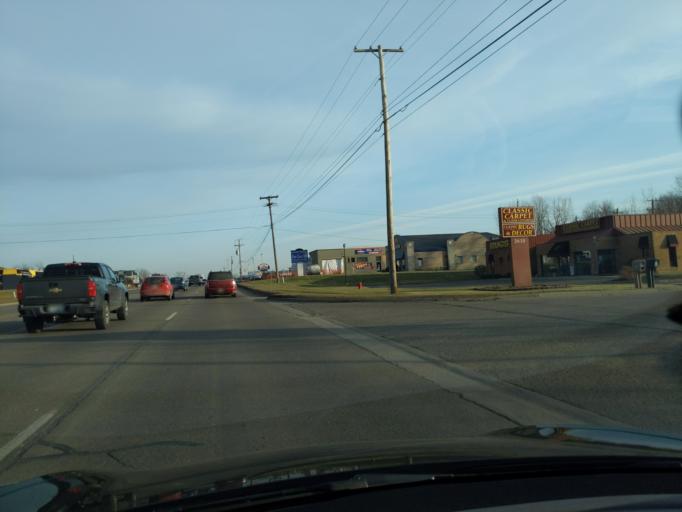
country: US
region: Michigan
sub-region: Livingston County
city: Howell
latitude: 42.5972
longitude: -83.9030
